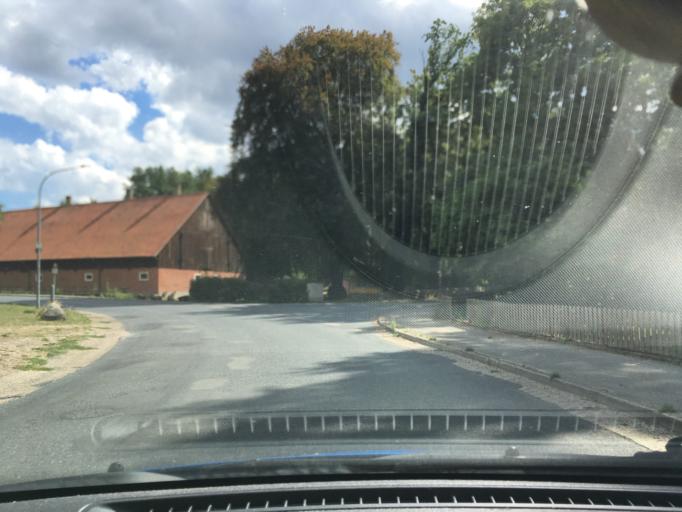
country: DE
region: Lower Saxony
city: Rehlingen
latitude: 53.0619
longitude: 10.2340
